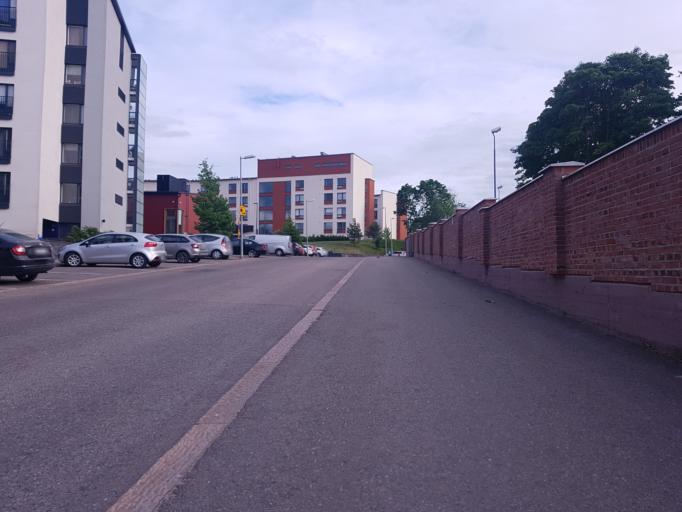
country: FI
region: Uusimaa
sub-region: Helsinki
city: Helsinki
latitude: 60.1947
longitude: 24.9726
